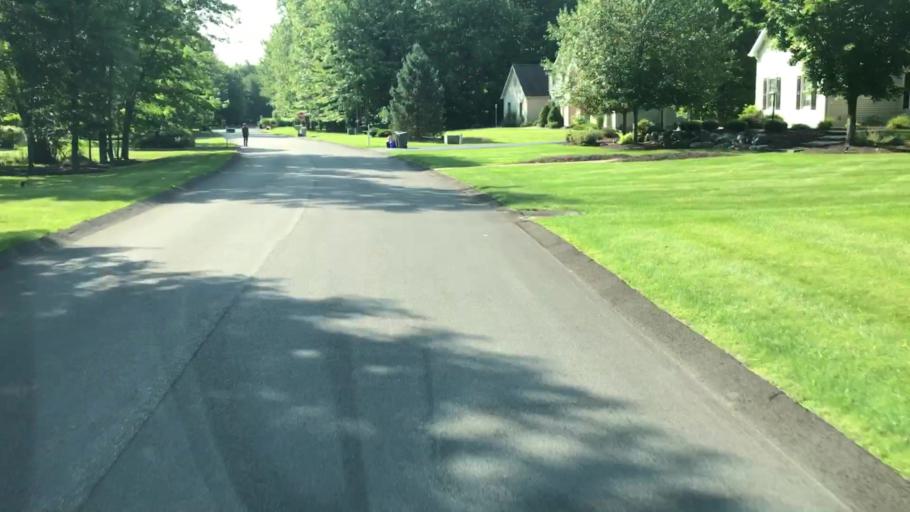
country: US
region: New York
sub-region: Onondaga County
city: Manlius
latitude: 42.9886
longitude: -75.9774
